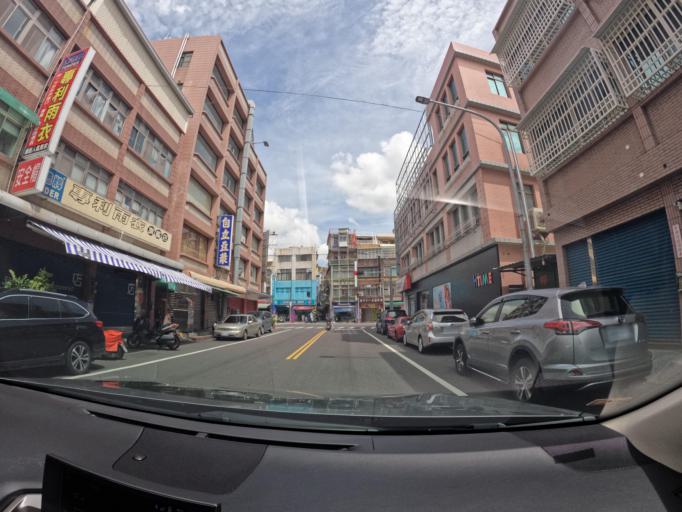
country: TW
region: Kaohsiung
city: Kaohsiung
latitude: 22.6865
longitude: 120.2907
